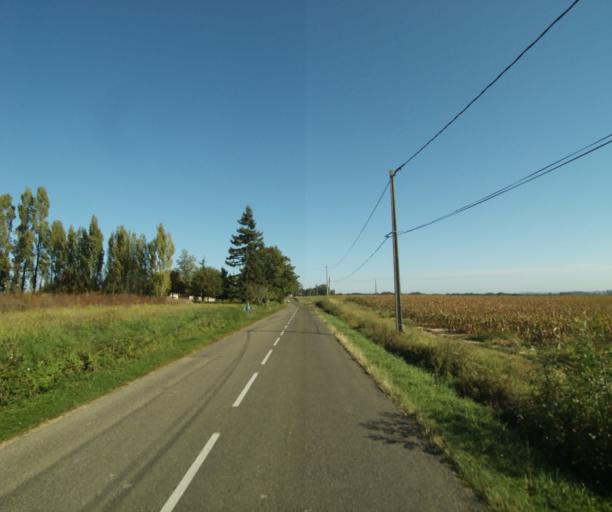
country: FR
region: Aquitaine
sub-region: Departement des Landes
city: Gabarret
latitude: 43.9217
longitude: 0.0172
